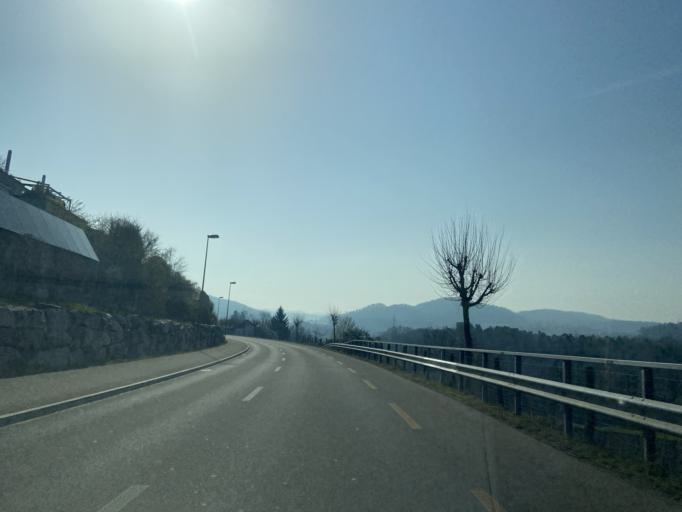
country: CH
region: Zurich
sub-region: Bezirk Winterthur
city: Neftenbach / Dorf Neftenbach
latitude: 47.5201
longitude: 8.6716
